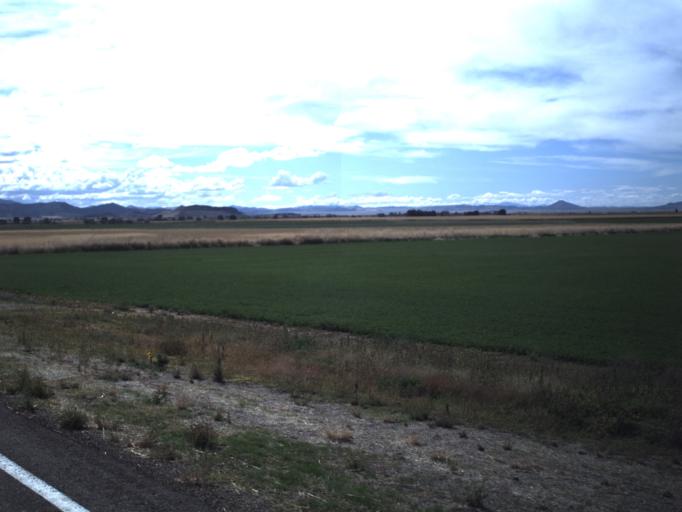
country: US
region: Utah
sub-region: Millard County
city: Fillmore
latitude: 38.8582
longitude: -112.4198
